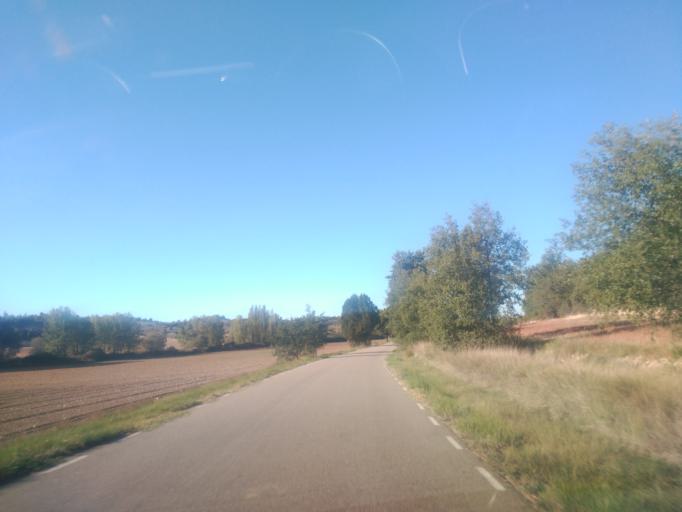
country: ES
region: Castille and Leon
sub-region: Provincia de Burgos
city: Brazacorta
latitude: 41.6937
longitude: -3.4044
